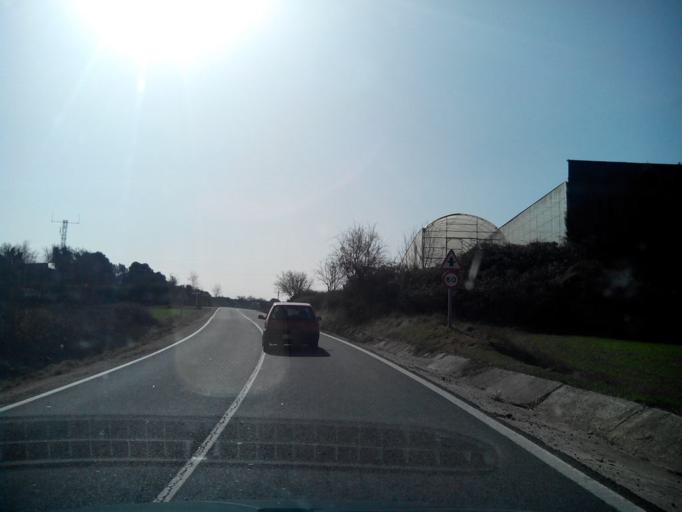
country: ES
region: Catalonia
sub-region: Provincia de Tarragona
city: Conesa
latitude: 41.5032
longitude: 1.3393
